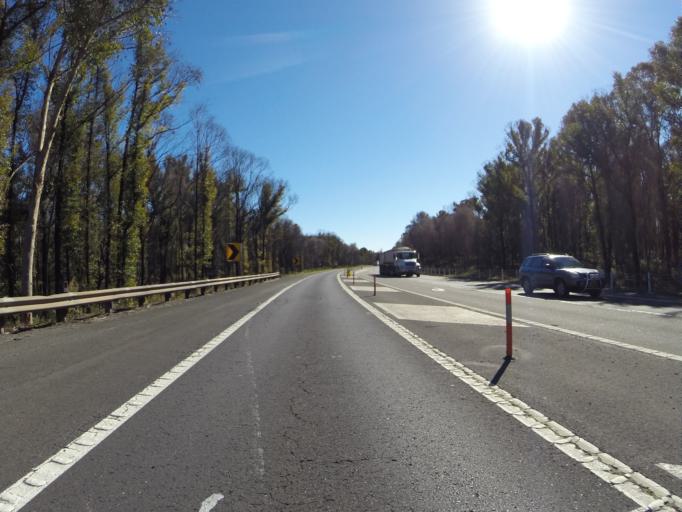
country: AU
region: New South Wales
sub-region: Wollondilly
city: Douglas Park
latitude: -34.3086
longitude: 150.7390
